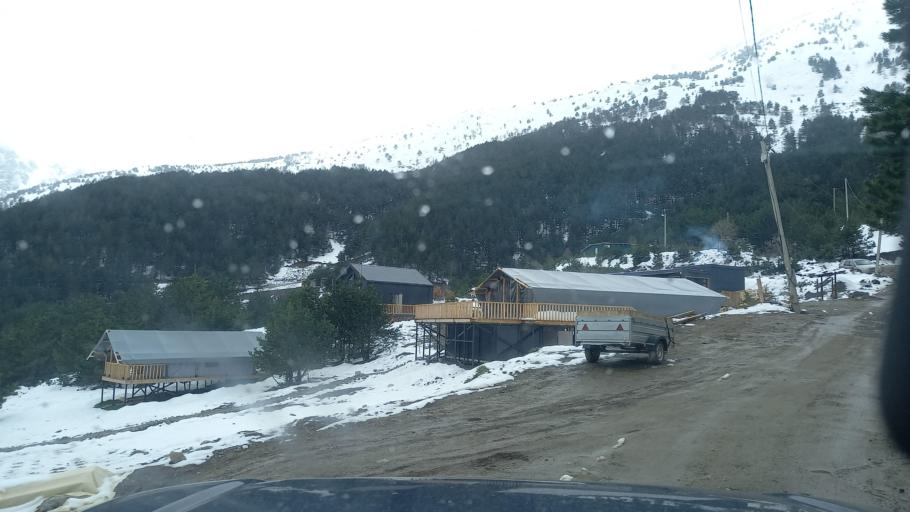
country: RU
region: North Ossetia
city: Mizur
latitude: 42.8093
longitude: 43.9570
